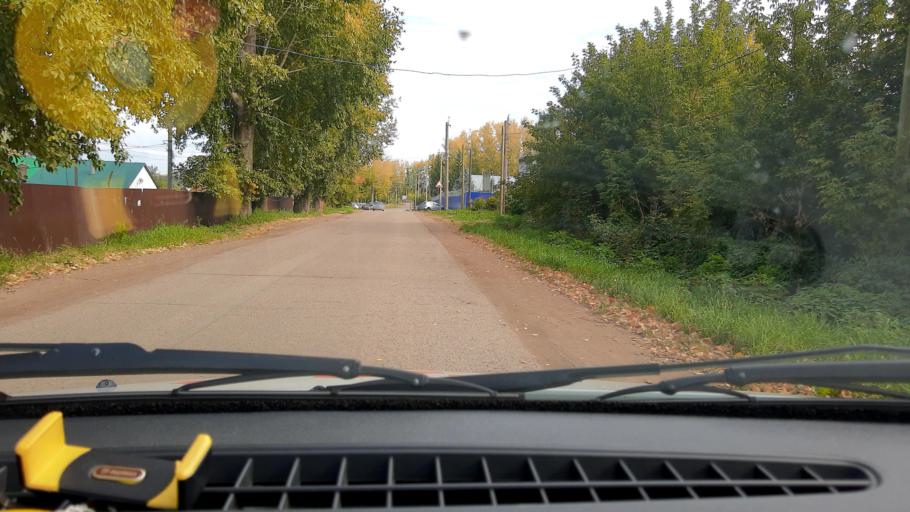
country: RU
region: Bashkortostan
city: Blagoveshchensk
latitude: 55.0436
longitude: 55.9842
